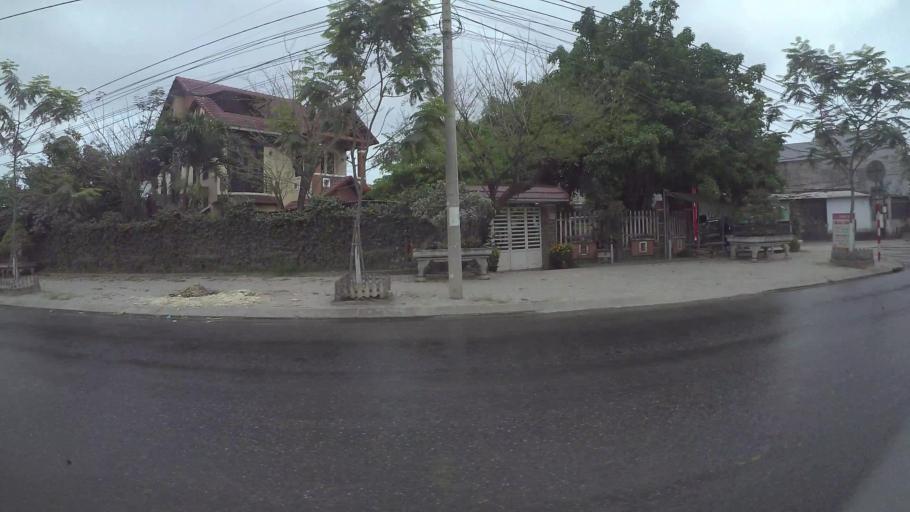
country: VN
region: Da Nang
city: Cam Le
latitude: 16.0351
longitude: 108.1738
